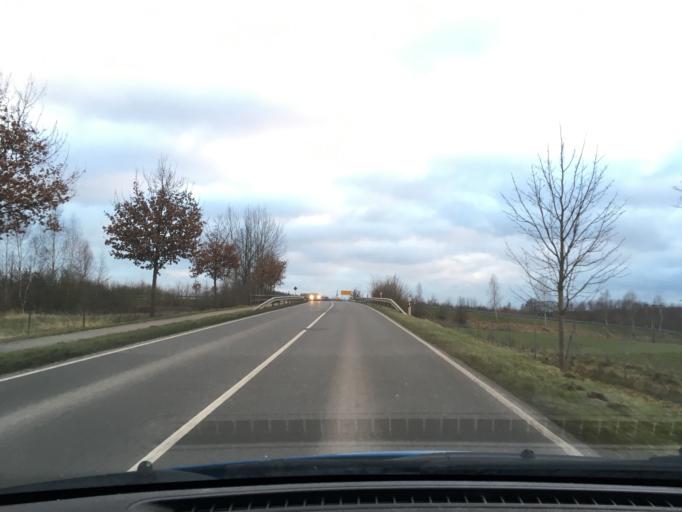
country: DE
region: Lower Saxony
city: Wrestedt
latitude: 52.9183
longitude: 10.5290
